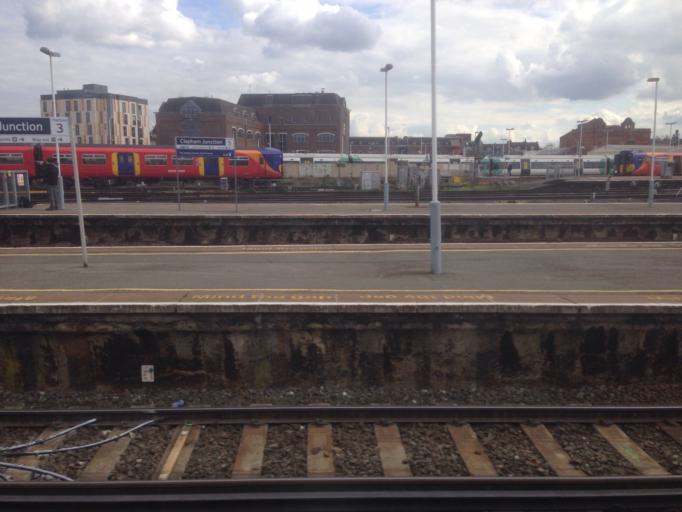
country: GB
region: England
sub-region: Greater London
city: Battersea
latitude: 51.4654
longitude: -0.1695
